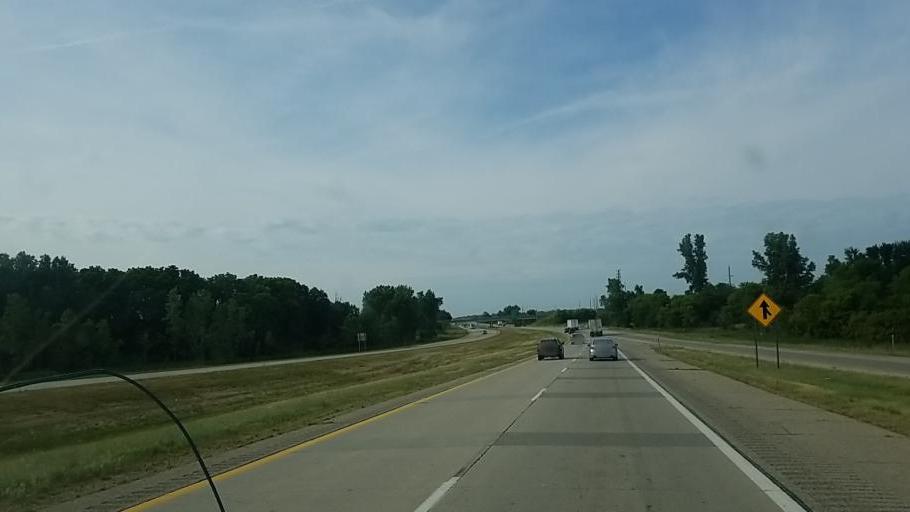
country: US
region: Michigan
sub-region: Eaton County
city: Charlotte
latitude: 42.5730
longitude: -84.8205
